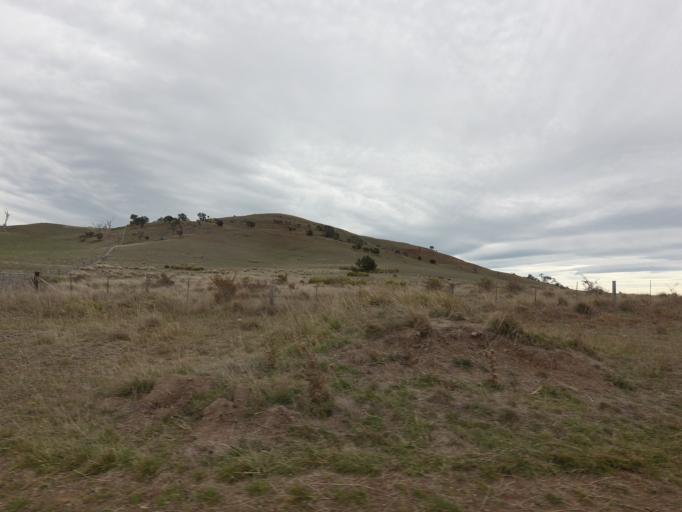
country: AU
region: Tasmania
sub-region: Derwent Valley
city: New Norfolk
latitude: -42.3732
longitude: 146.8611
